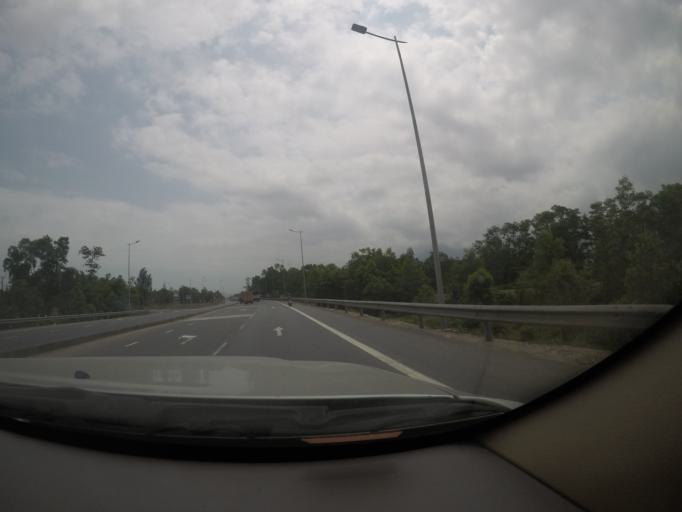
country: VN
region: Thua Thien-Hue
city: Phu Loc
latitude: 16.2731
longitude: 107.9240
